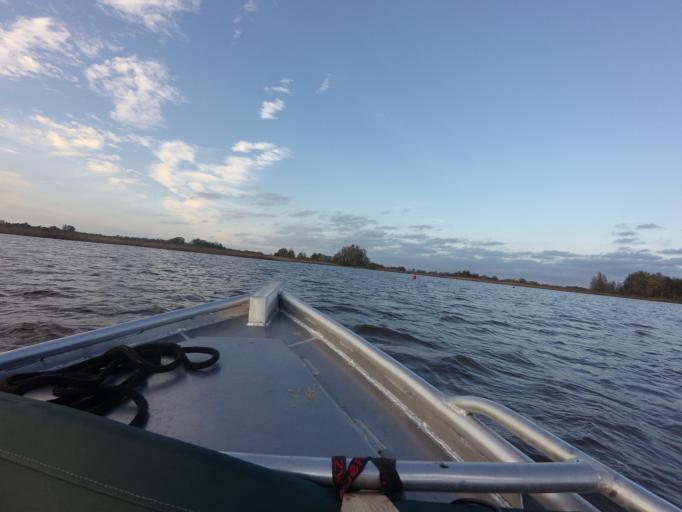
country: NL
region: Overijssel
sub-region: Gemeente Steenwijkerland
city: Blokzijl
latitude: 52.7354
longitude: 5.9947
